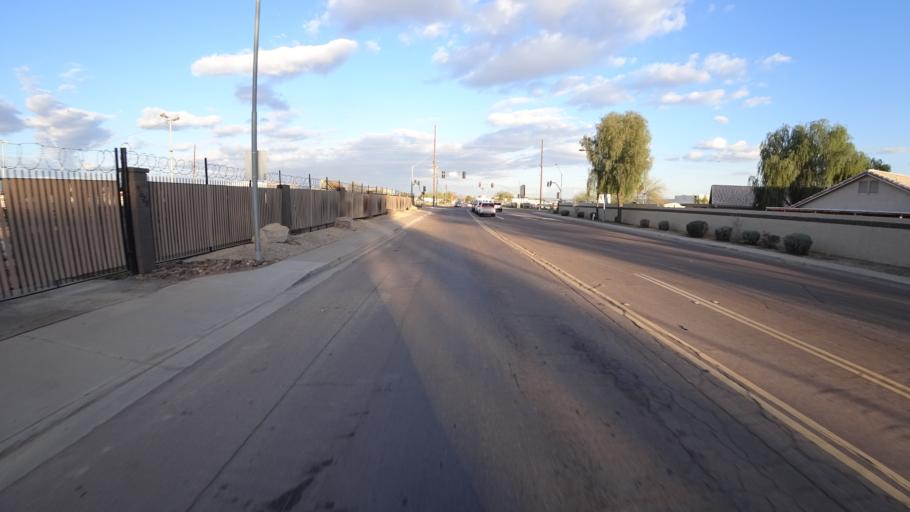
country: US
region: Arizona
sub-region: Maricopa County
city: Glendale
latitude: 33.5456
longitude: -112.2038
